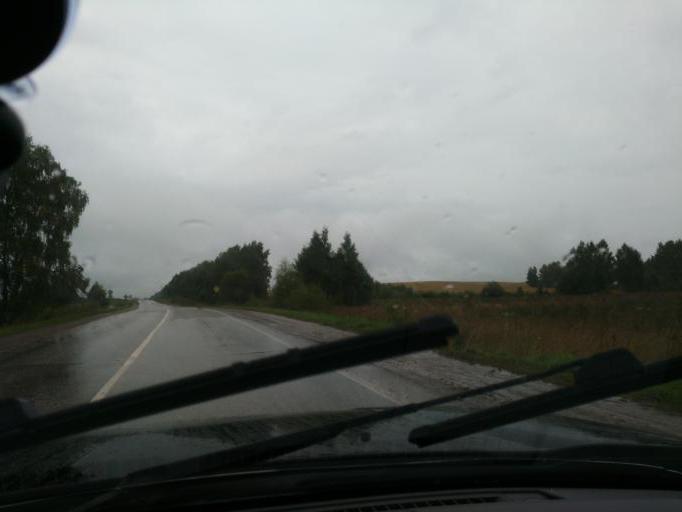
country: RU
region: Perm
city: Osa
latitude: 57.3743
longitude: 55.6097
